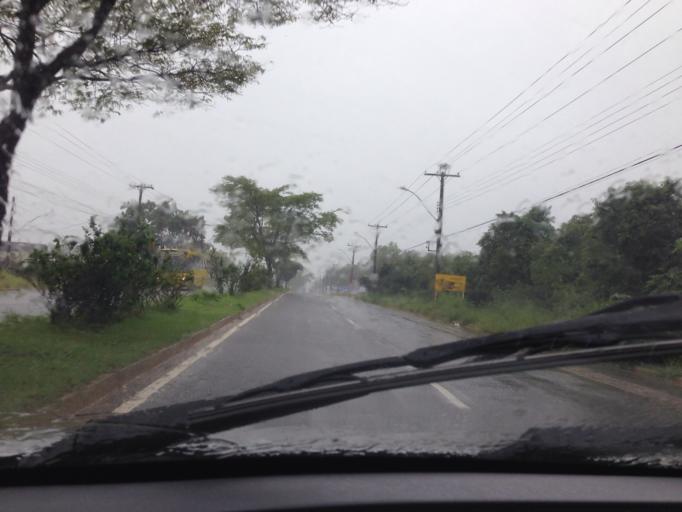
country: BR
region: Espirito Santo
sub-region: Guarapari
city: Guarapari
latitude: -20.6480
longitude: -40.5108
